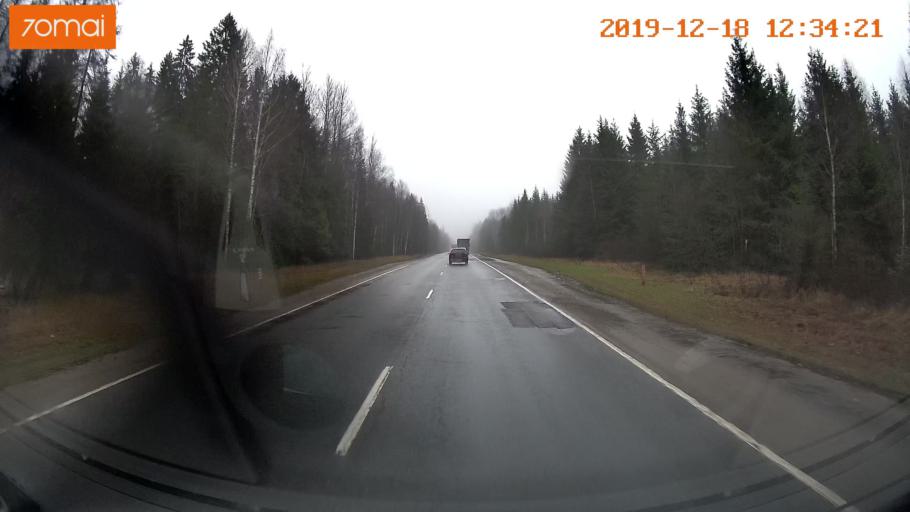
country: RU
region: Moskovskaya
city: Rumyantsevo
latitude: 56.1204
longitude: 36.5711
